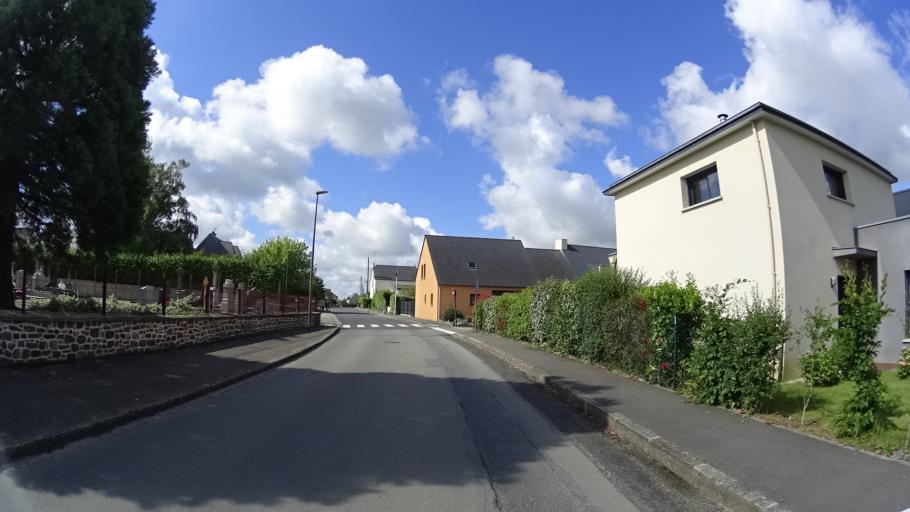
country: FR
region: Brittany
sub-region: Departement d'Ille-et-Vilaine
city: Saint-Gilles
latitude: 48.1291
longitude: -1.8184
